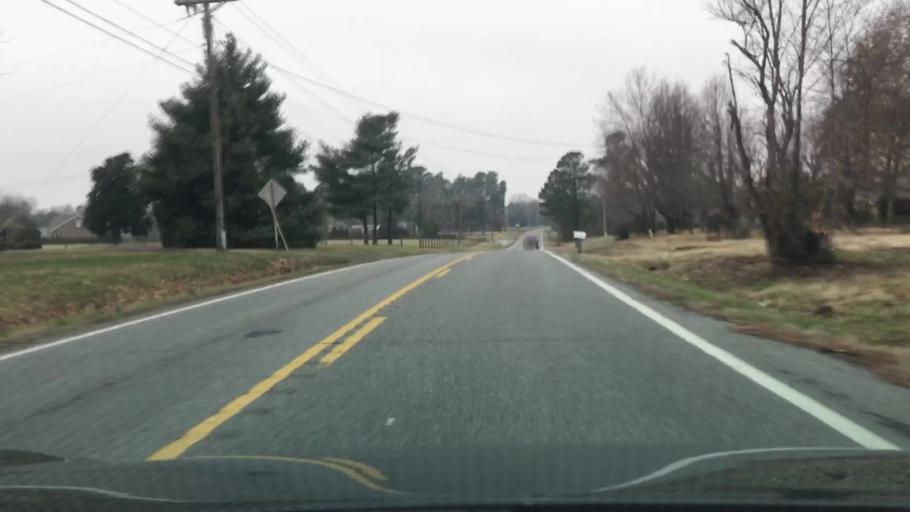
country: US
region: Kentucky
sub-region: Livingston County
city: Ledbetter
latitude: 36.9671
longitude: -88.4515
